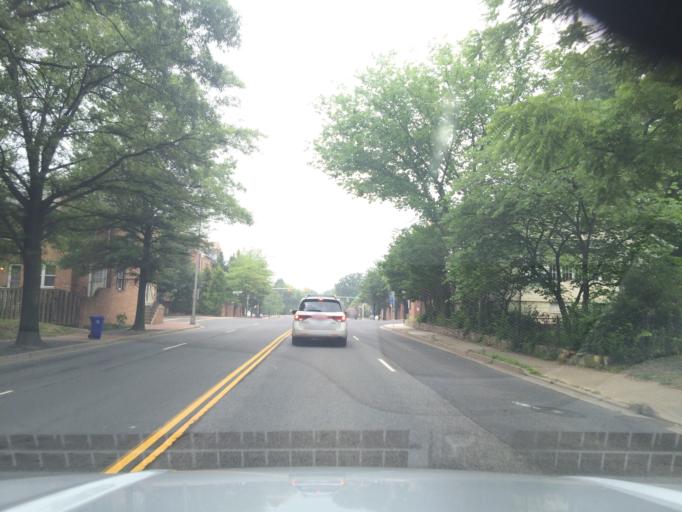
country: US
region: Virginia
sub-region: Arlington County
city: Arlington
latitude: 38.8855
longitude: -77.1153
